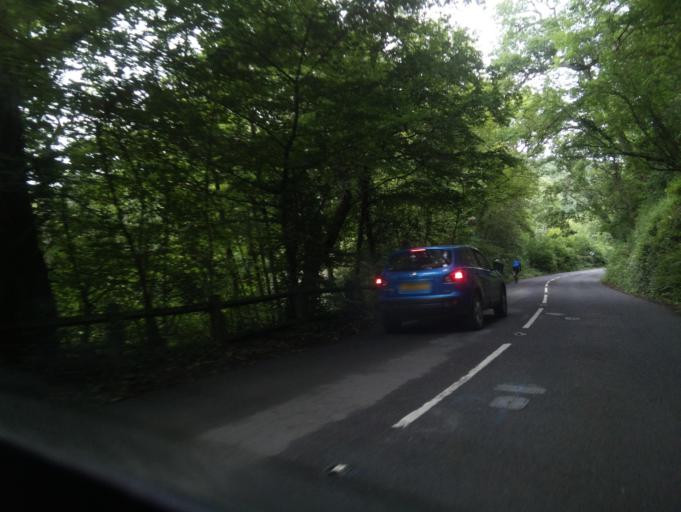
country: GB
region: England
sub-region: Devon
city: Chudleigh
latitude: 50.6656
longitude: -3.6448
